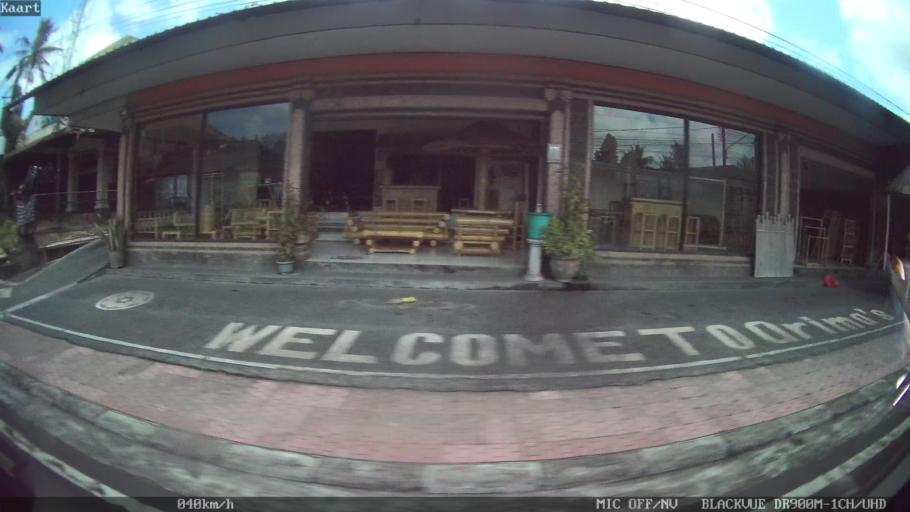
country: ID
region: Bali
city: Banjar Desa
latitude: -8.5743
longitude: 115.2763
